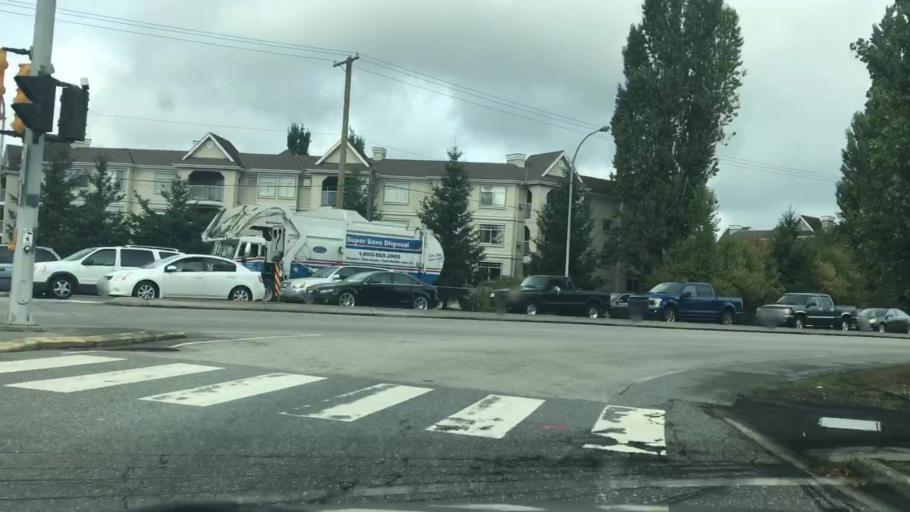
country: CA
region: British Columbia
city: Langley
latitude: 49.1047
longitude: -122.6426
